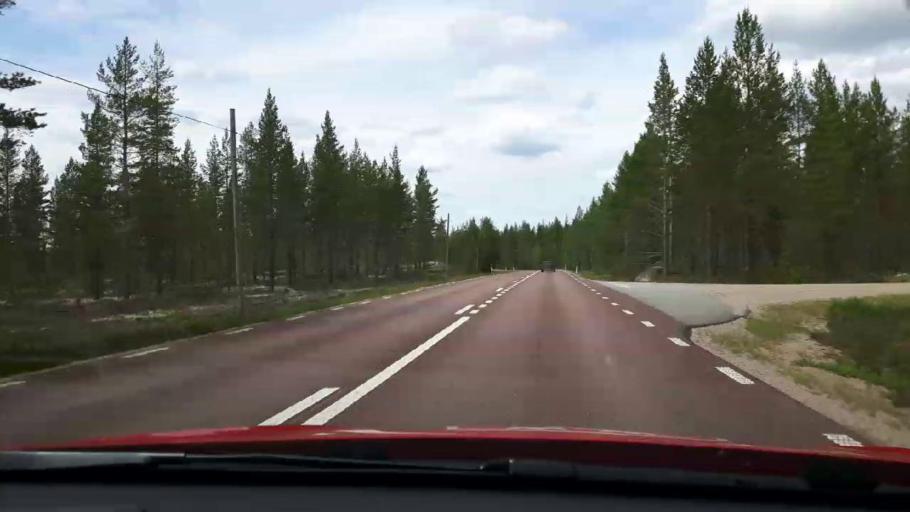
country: SE
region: Jaemtland
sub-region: Harjedalens Kommun
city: Sveg
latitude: 62.0577
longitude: 14.5908
